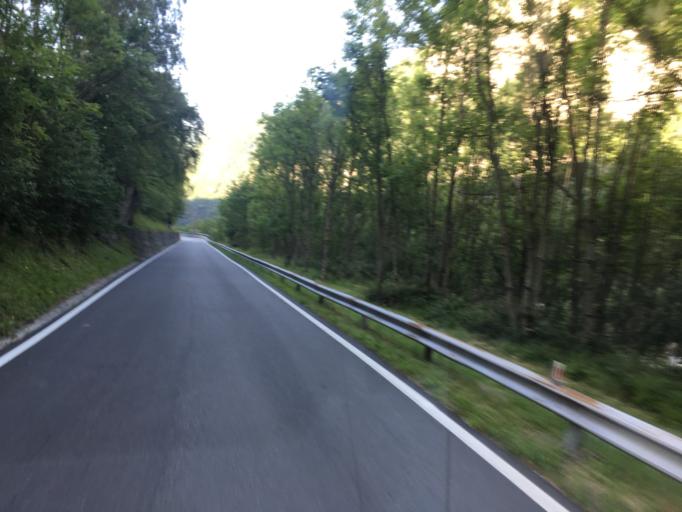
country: IT
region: Lombardy
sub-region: Provincia di Sondrio
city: San Giacomo Filippo
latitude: 46.3659
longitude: 9.3638
